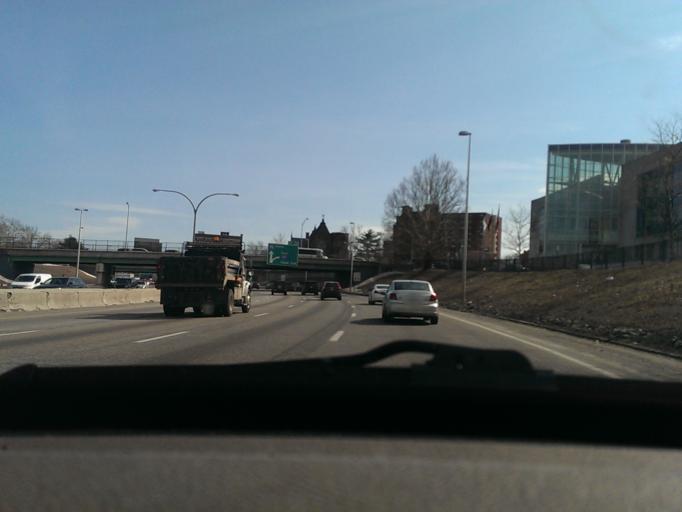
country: US
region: Rhode Island
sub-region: Providence County
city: Providence
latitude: 41.8208
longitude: -71.4202
